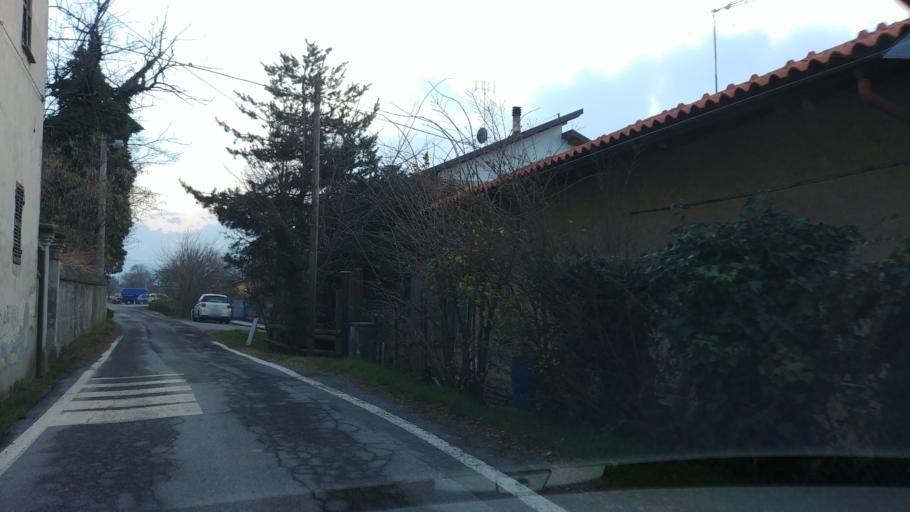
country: IT
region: Piedmont
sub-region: Provincia di Cuneo
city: Cuneo
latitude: 44.3975
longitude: 7.5790
